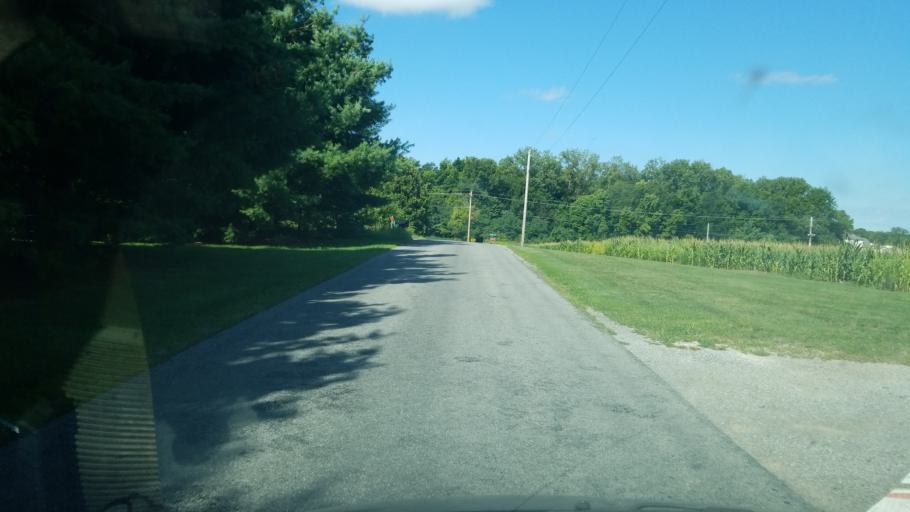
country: US
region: Ohio
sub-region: Wood County
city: North Baltimore
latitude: 41.1242
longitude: -83.7062
